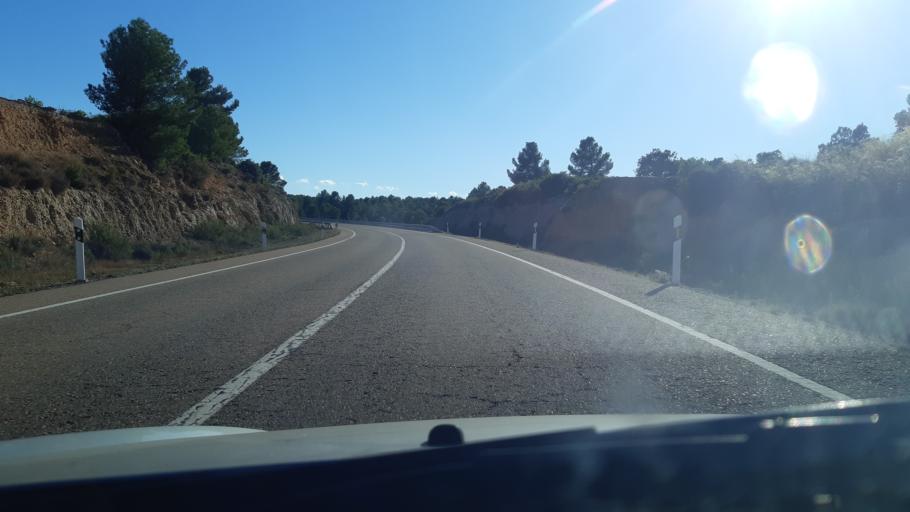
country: ES
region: Aragon
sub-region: Provincia de Teruel
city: Fornoles
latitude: 40.9244
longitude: -0.0189
